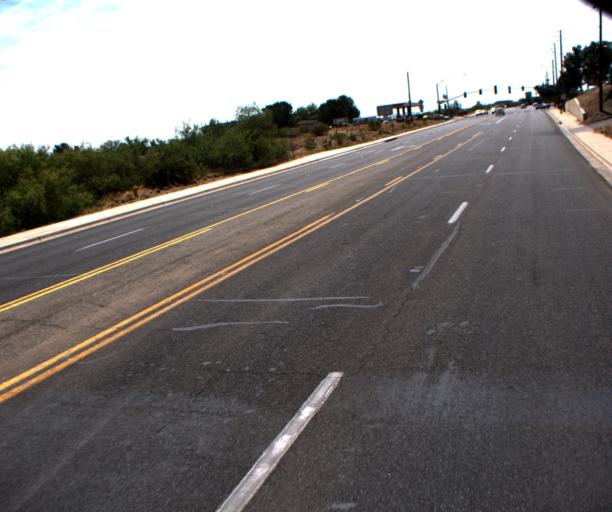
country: US
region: Arizona
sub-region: Yavapai County
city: Cottonwood
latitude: 34.7391
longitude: -112.0366
